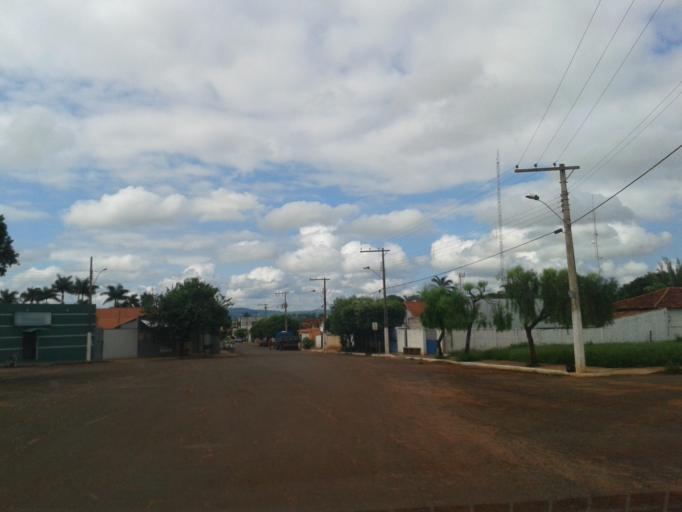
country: BR
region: Minas Gerais
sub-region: Ituiutaba
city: Ituiutaba
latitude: -19.2086
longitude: -49.7849
